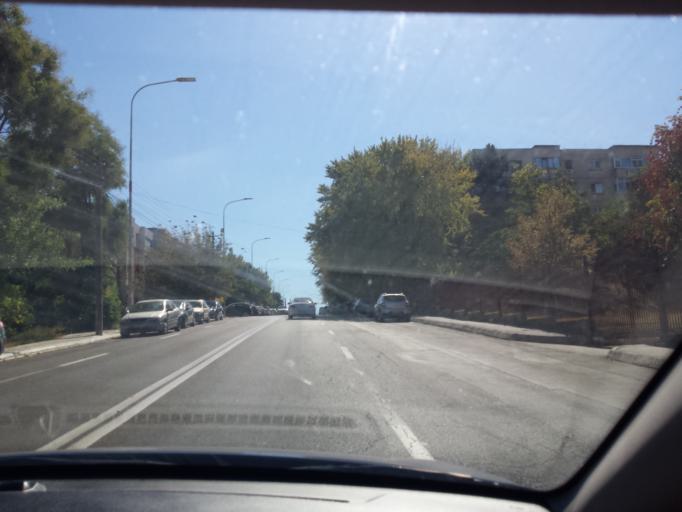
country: RO
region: Tulcea
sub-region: Municipiul Tulcea
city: Tulcea
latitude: 45.1665
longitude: 28.7938
